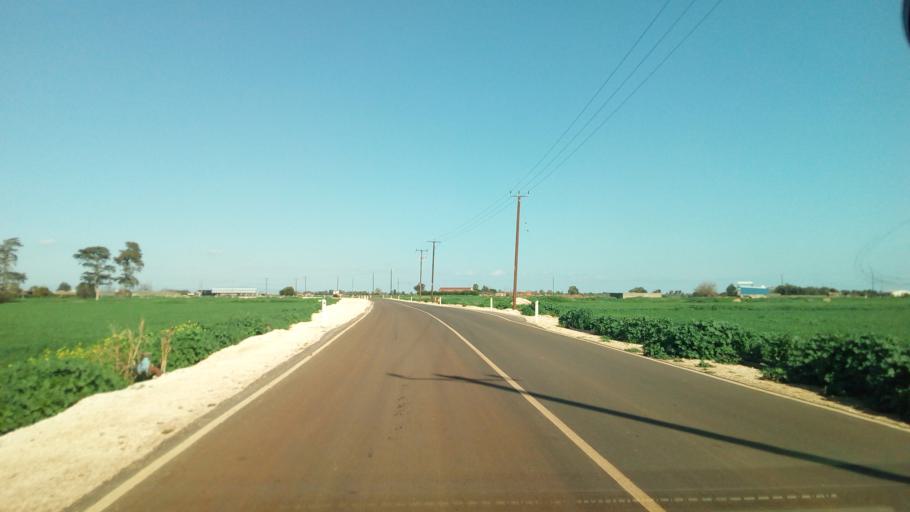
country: CY
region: Ammochostos
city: Avgorou
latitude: 35.0065
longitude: 33.8450
